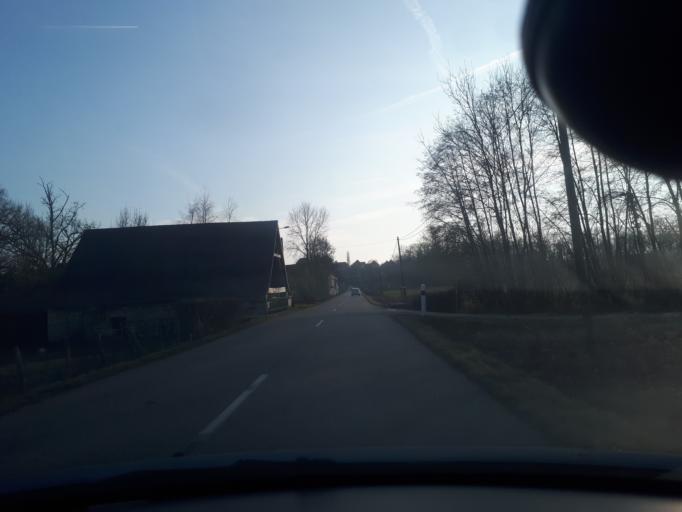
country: FR
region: Rhone-Alpes
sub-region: Departement de l'Isere
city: Creys-Mepieu
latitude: 45.6999
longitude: 5.5314
